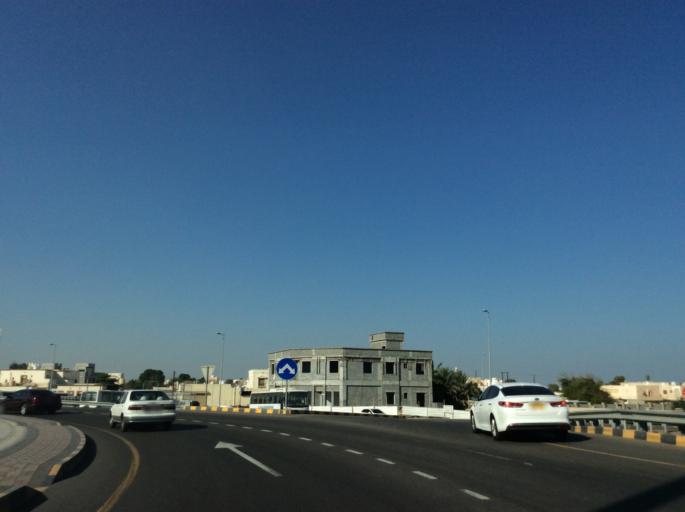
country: OM
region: Al Batinah
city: Al Liwa'
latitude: 24.4242
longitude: 56.6117
